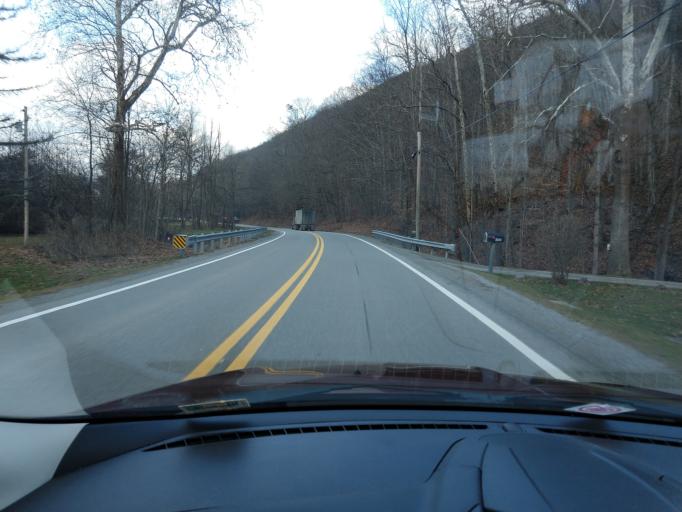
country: US
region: West Virginia
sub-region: Randolph County
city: Elkins
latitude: 38.6743
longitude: -79.9517
